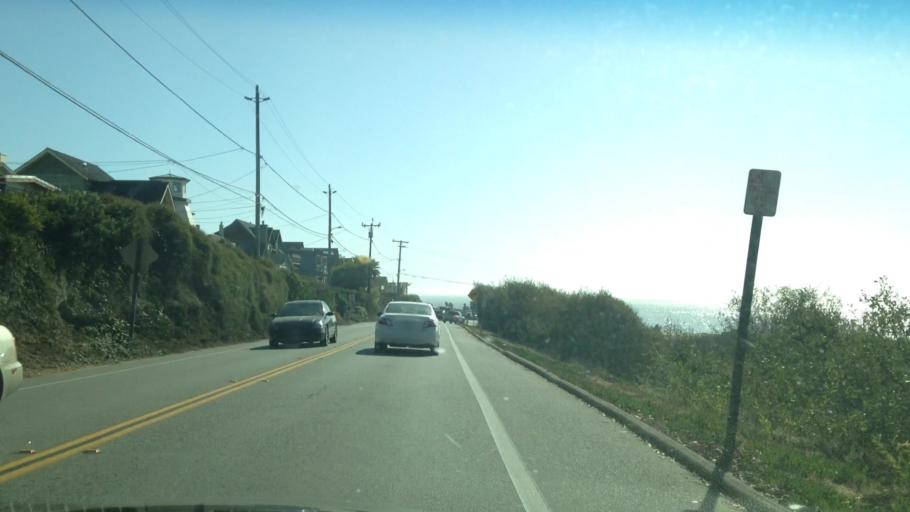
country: US
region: California
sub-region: Santa Cruz County
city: Twin Lakes
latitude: 36.9631
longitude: -121.9954
